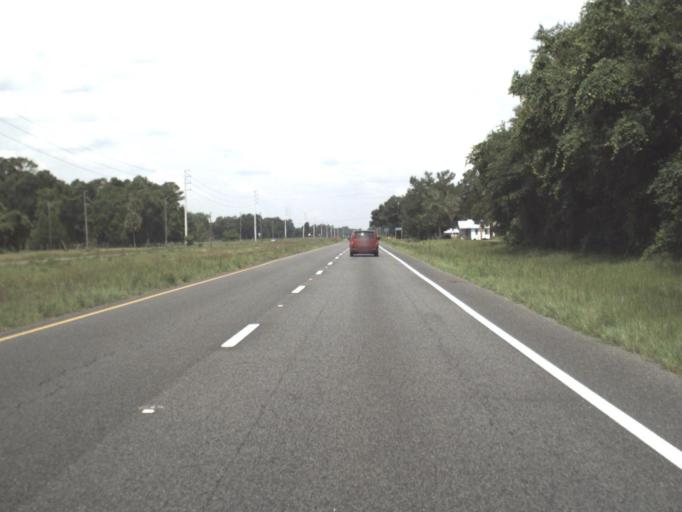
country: US
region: Florida
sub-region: Levy County
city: Chiefland
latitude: 29.4750
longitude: -82.8175
